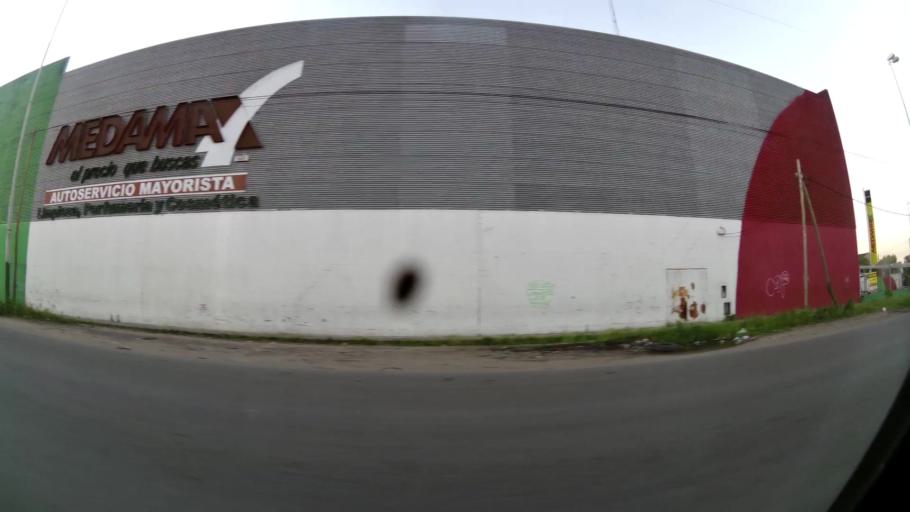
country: AR
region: Buenos Aires
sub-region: Partido de Almirante Brown
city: Adrogue
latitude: -34.7958
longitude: -58.3196
